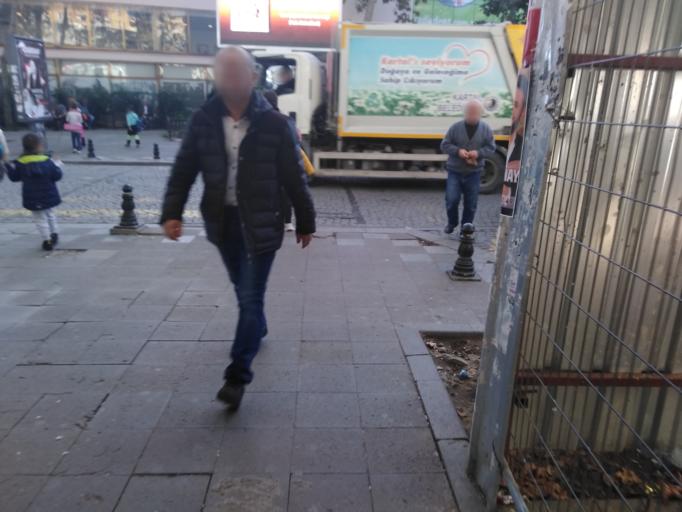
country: TR
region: Istanbul
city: Maltepe
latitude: 40.8895
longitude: 29.1895
